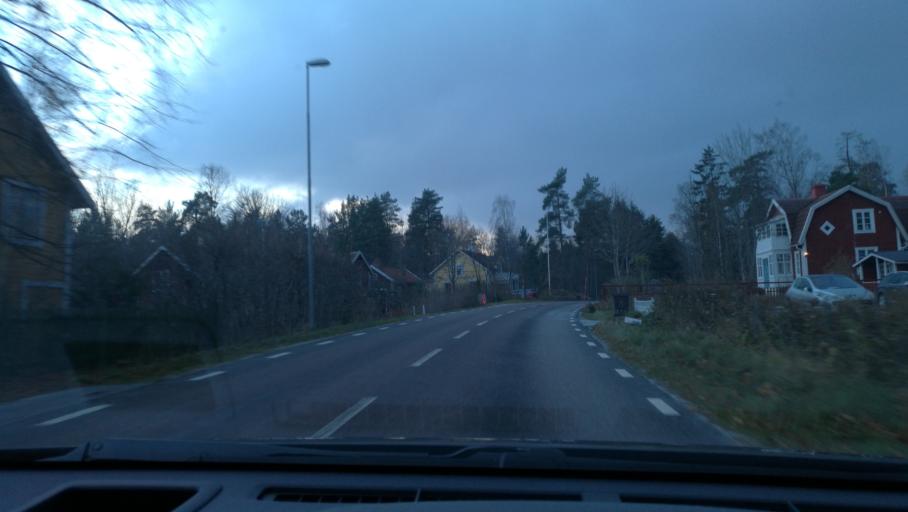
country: SE
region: Soedermanland
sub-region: Vingakers Kommun
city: Vingaker
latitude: 59.1315
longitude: 15.8202
